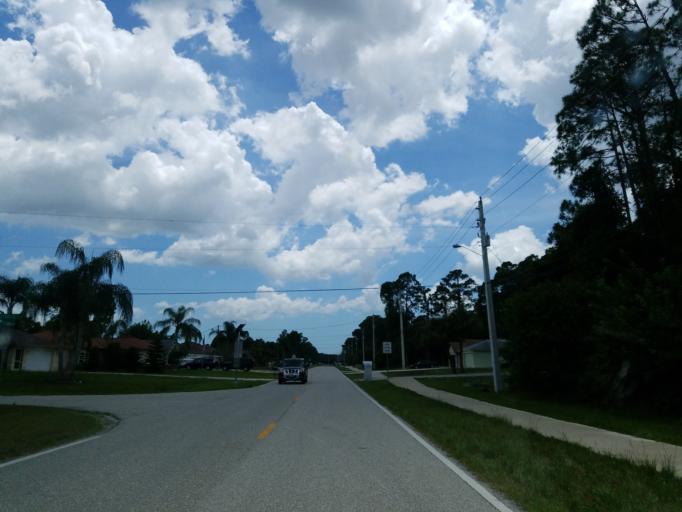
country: US
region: Florida
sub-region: Sarasota County
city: North Port
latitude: 27.0895
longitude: -82.1779
